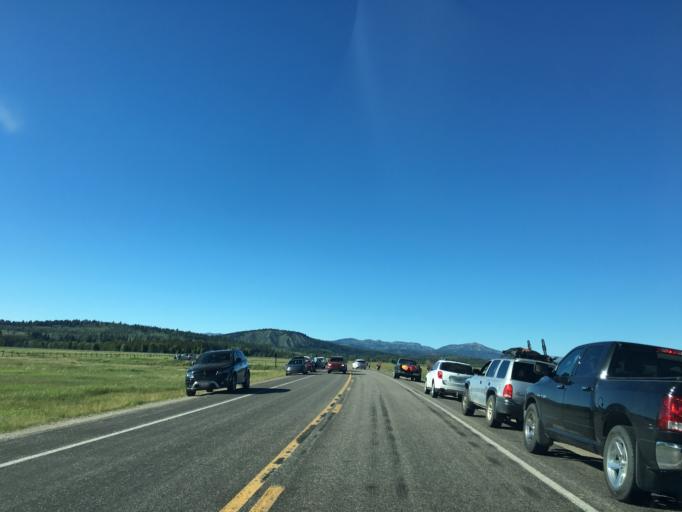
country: US
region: Wyoming
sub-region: Teton County
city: Jackson
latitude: 43.8092
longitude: -110.5269
